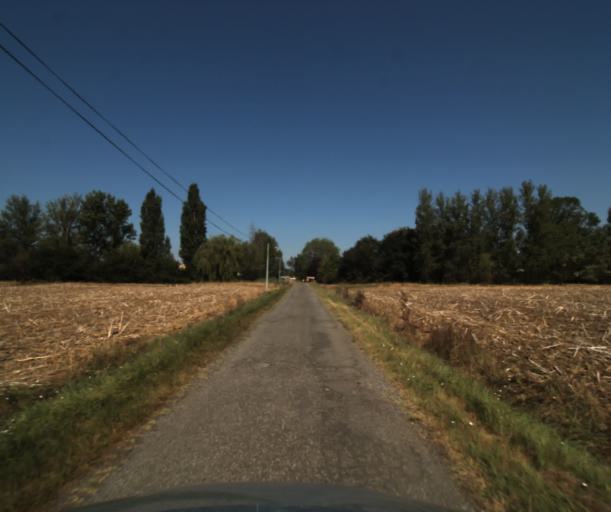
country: FR
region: Midi-Pyrenees
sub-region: Departement de la Haute-Garonne
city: Labastidette
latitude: 43.4533
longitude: 1.2481
